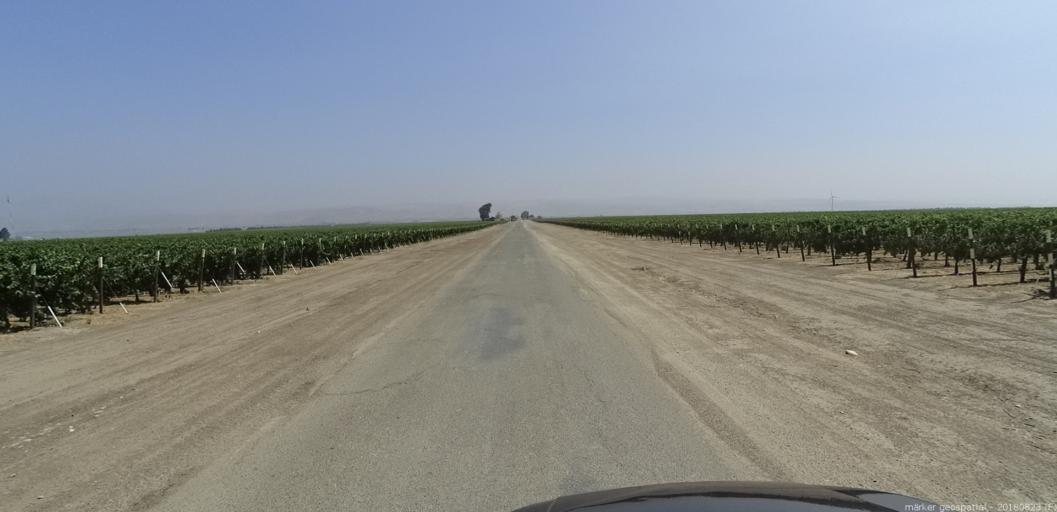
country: US
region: California
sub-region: Monterey County
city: Greenfield
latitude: 36.2734
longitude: -121.2202
